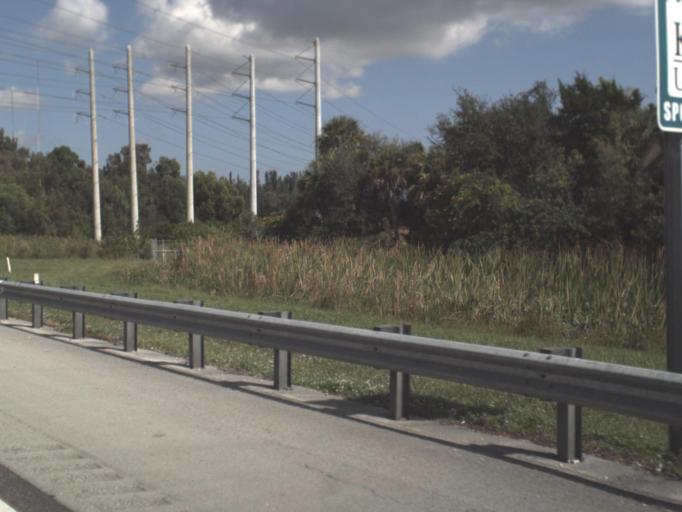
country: US
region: Florida
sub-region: Palm Beach County
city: Schall Circle
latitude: 26.7445
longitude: -80.1346
